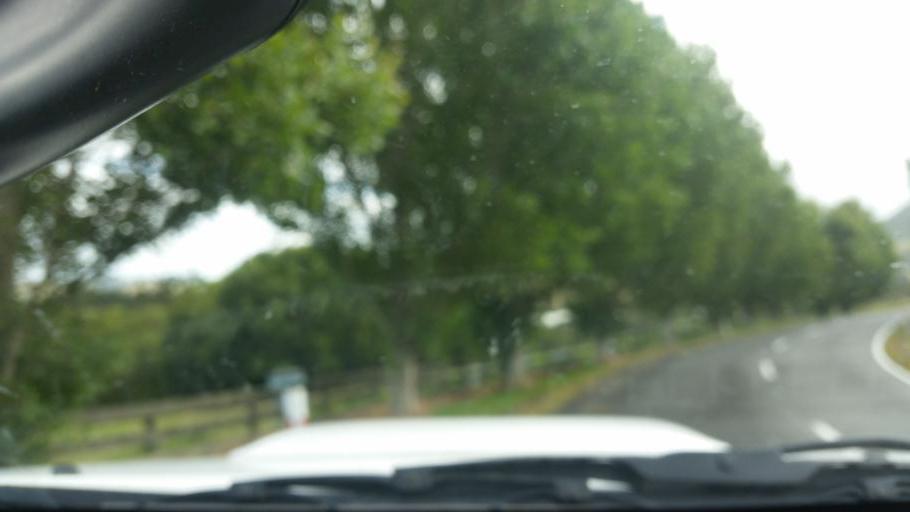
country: NZ
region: Auckland
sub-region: Auckland
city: Wellsford
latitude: -36.1311
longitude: 174.3657
